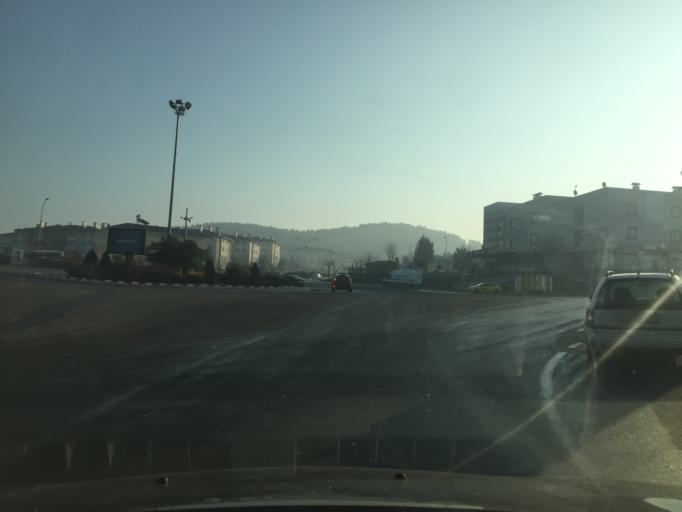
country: TR
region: Duzce
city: Duzce
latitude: 40.8683
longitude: 31.2262
